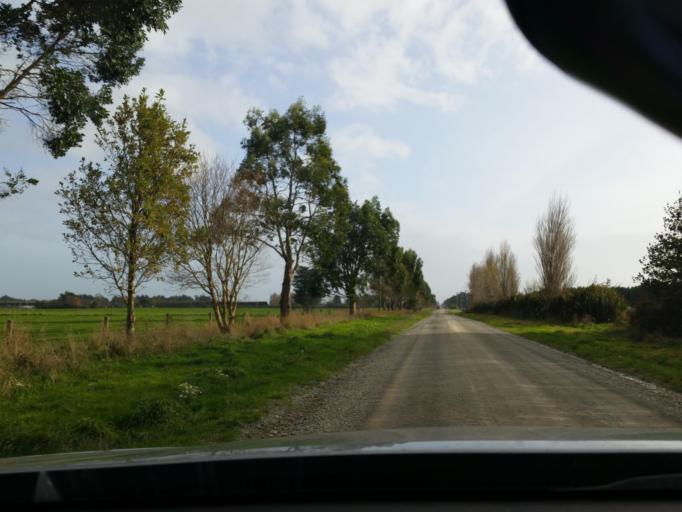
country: NZ
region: Southland
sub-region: Southland District
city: Winton
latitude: -46.2268
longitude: 168.3277
